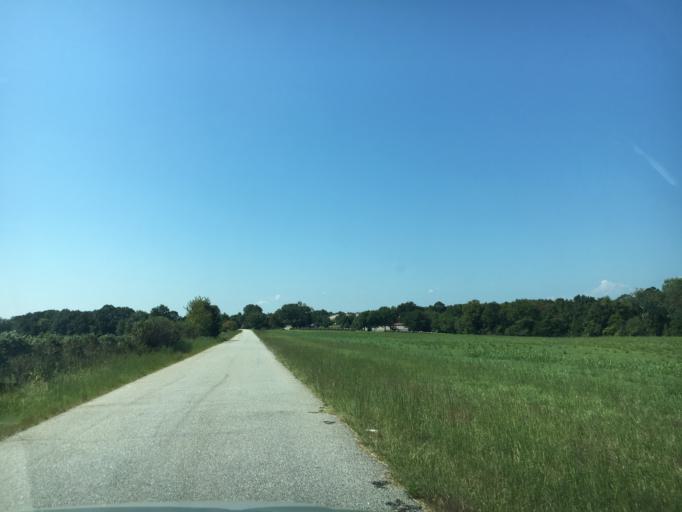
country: US
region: South Carolina
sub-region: Spartanburg County
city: Valley Falls
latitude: 35.0234
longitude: -81.9342
